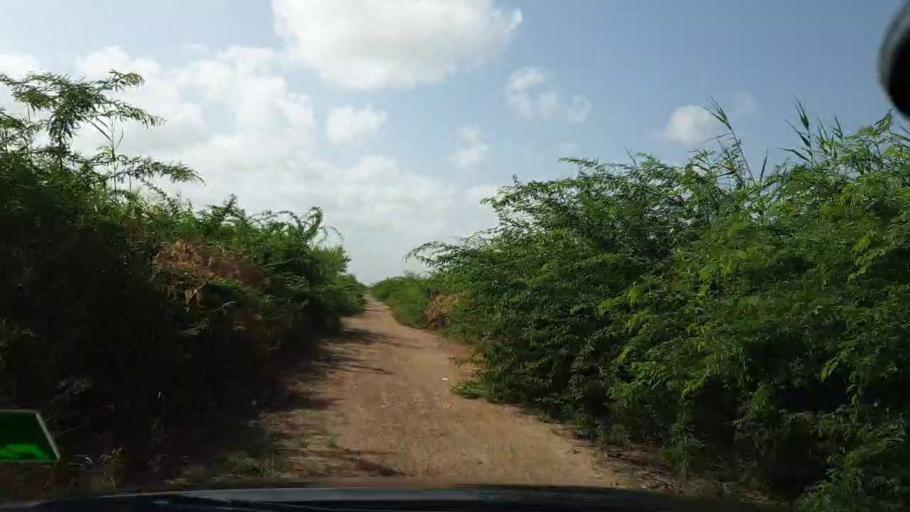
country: PK
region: Sindh
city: Kadhan
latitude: 24.6342
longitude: 69.1049
